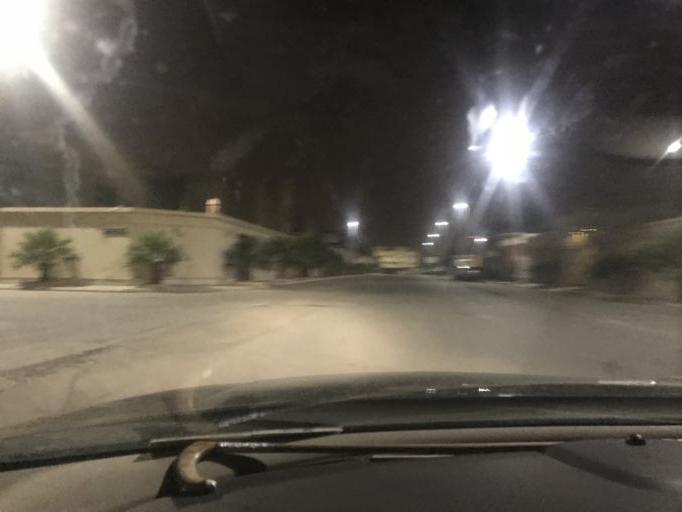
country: SA
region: Ar Riyad
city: Riyadh
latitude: 24.7338
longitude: 46.7803
